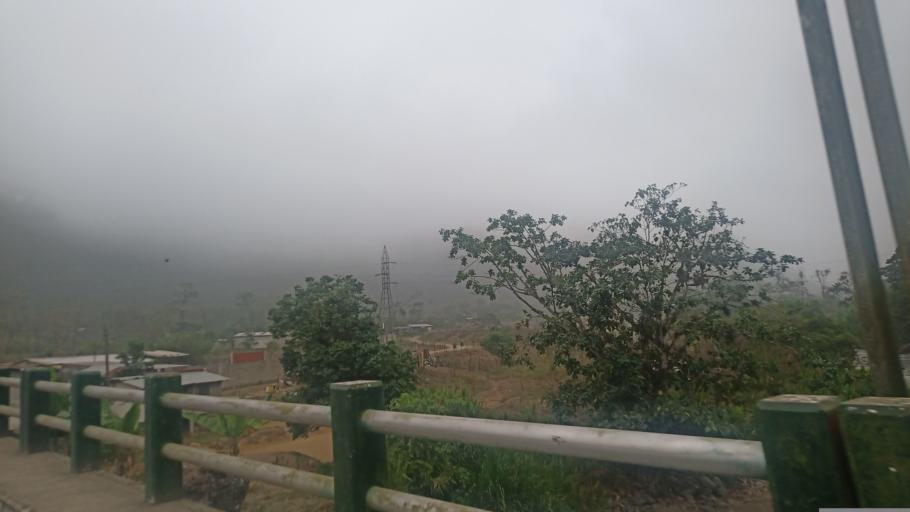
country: EC
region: Santo Domingo de los Tsachilas
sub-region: Canton Santo Domingo de los Colorados
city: Santo Domingo de los Colorados
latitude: -0.2769
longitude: -79.0761
